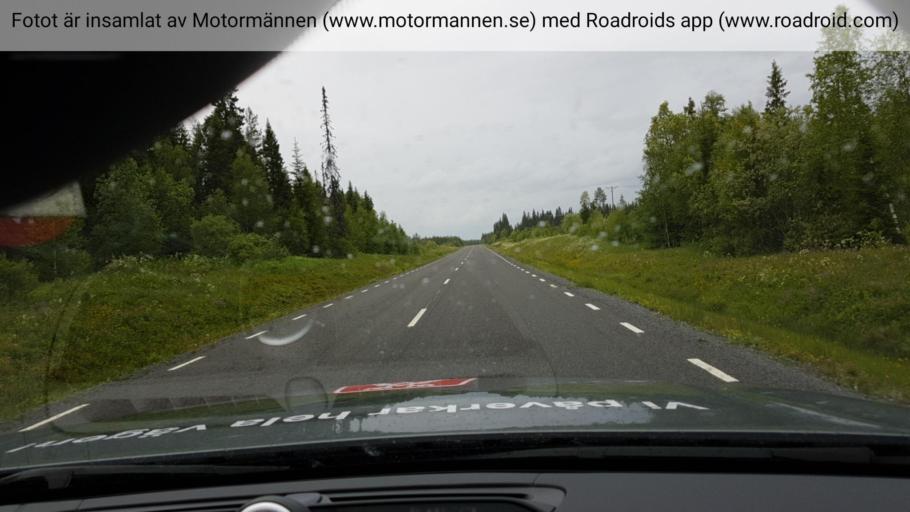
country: SE
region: Jaemtland
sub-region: Stroemsunds Kommun
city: Stroemsund
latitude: 63.6470
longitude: 15.1707
